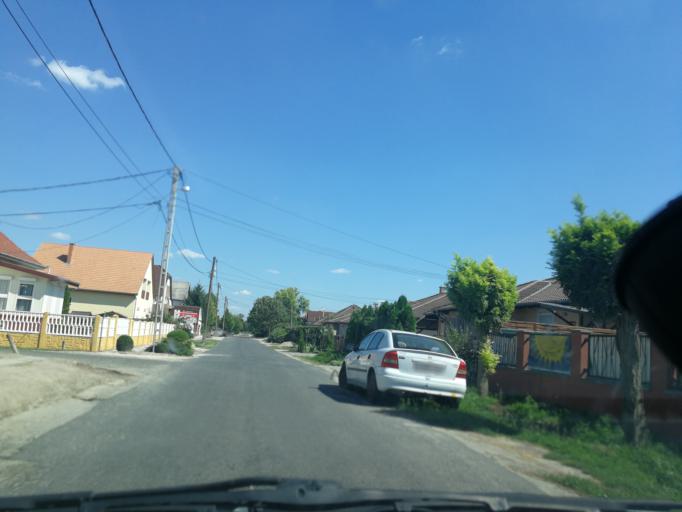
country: HU
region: Pest
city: Halasztelek
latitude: 47.3559
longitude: 18.9886
